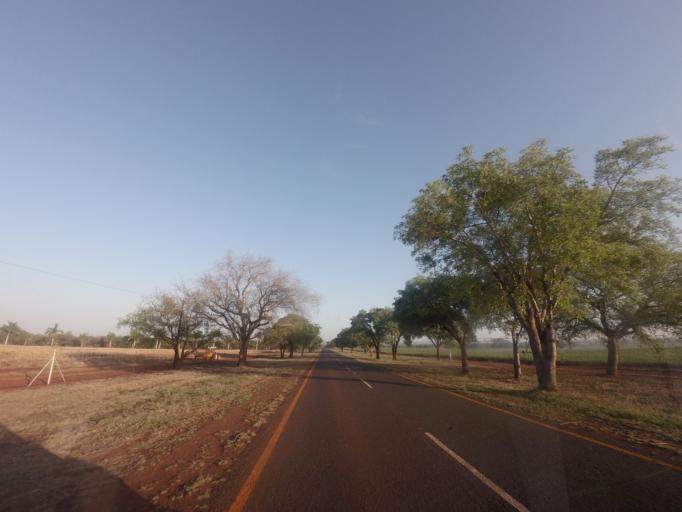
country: ZA
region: Mpumalanga
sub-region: Ehlanzeni District
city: Komatipoort
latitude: -25.3743
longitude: 31.9056
